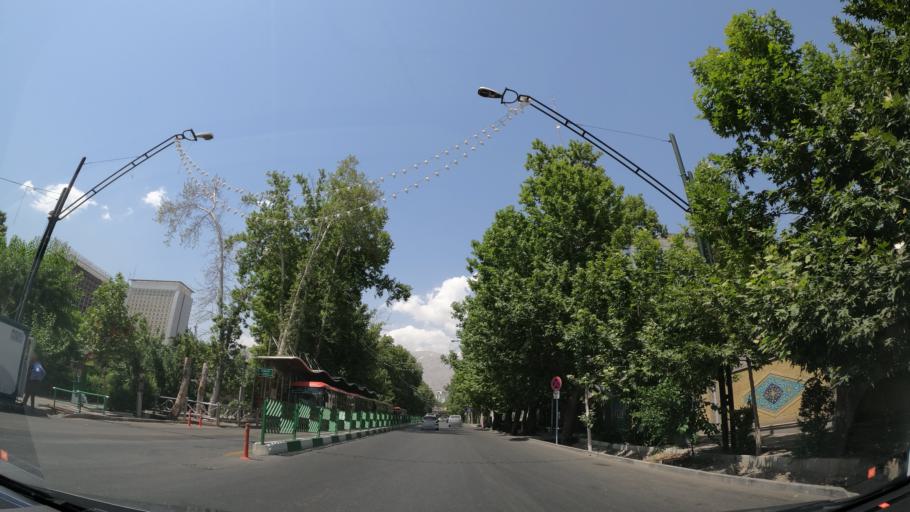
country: IR
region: Tehran
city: Tajrish
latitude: 35.7877
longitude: 51.4156
